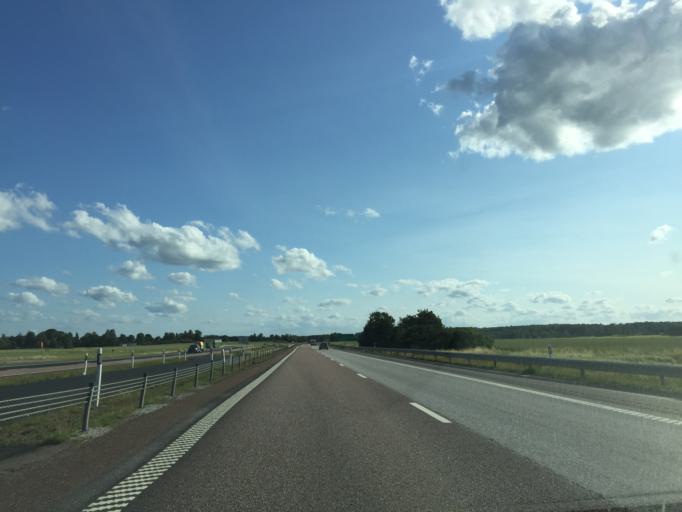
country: SE
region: OErebro
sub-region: Kumla Kommun
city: Kumla
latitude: 59.1614
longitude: 15.1069
